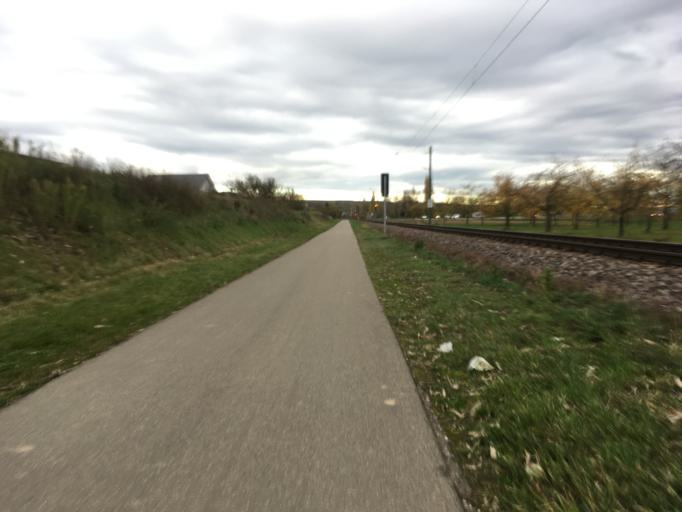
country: DE
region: Baden-Wuerttemberg
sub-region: Freiburg Region
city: Gottenheim
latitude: 48.0597
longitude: 7.7237
